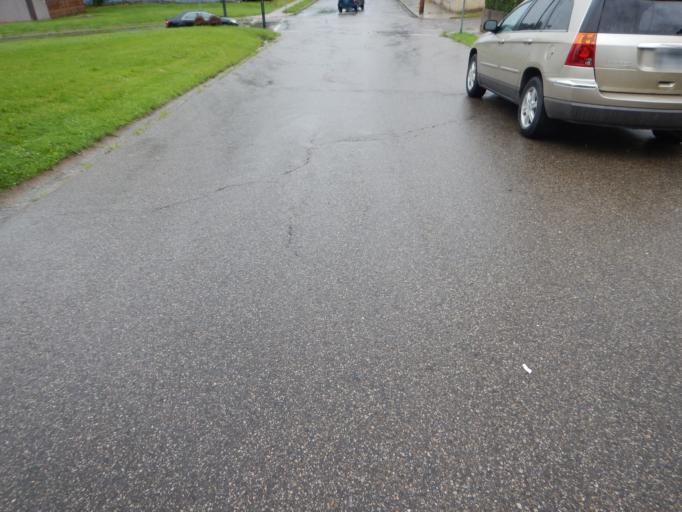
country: US
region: Ohio
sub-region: Muskingum County
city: Zanesville
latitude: 39.9328
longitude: -82.0188
